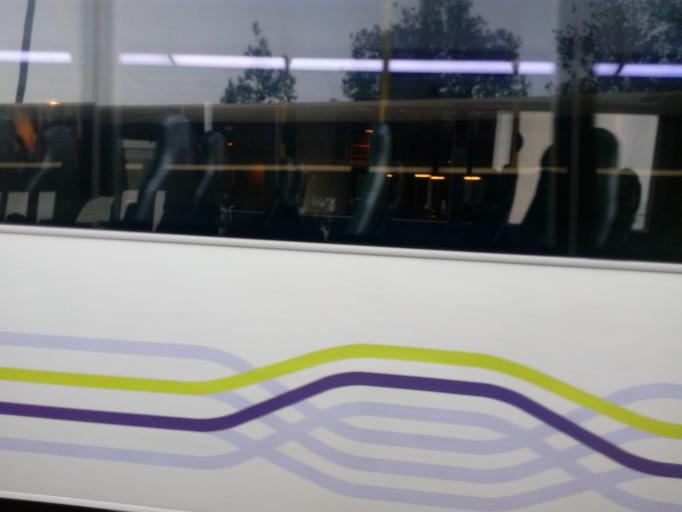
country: HK
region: Yuen Long
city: Yuen Long Kau Hui
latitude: 22.4465
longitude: 114.0358
